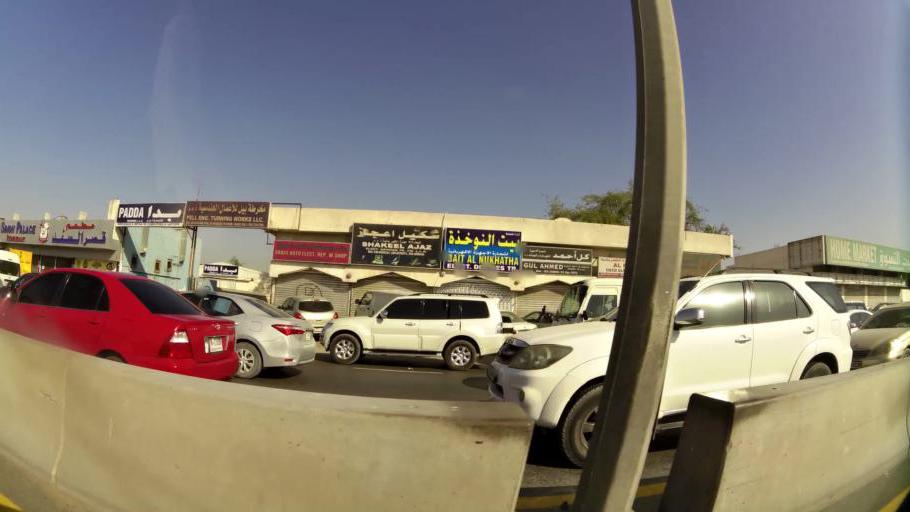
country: AE
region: Ash Shariqah
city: Sharjah
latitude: 25.3183
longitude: 55.4132
